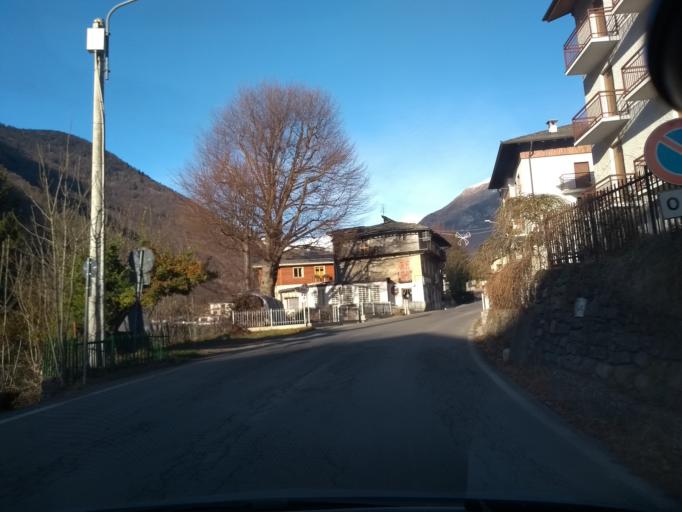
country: IT
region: Piedmont
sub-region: Provincia di Torino
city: Cantoira
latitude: 45.3452
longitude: 7.3763
